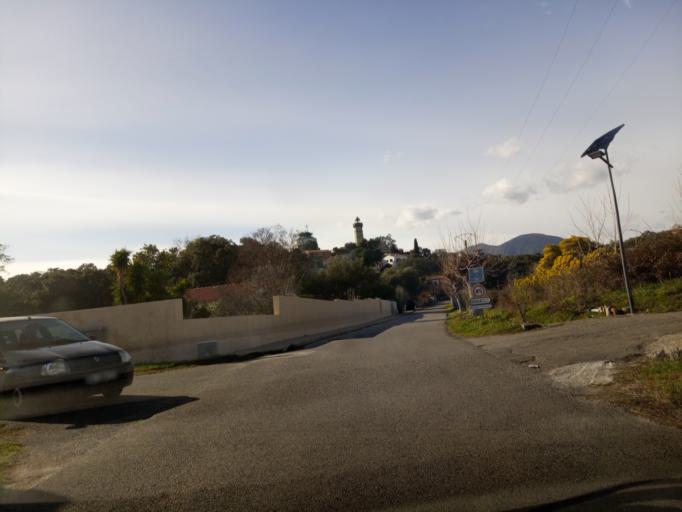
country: FR
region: Corsica
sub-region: Departement de la Haute-Corse
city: Linguizzetta
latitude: 42.2610
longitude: 9.5449
